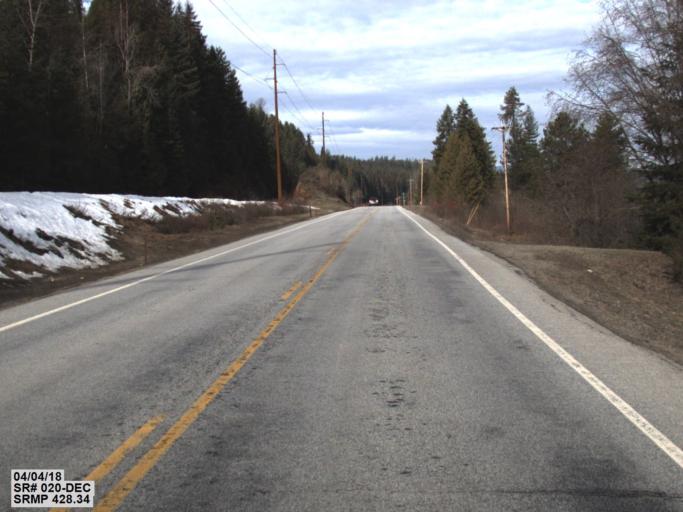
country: US
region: Washington
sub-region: Pend Oreille County
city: Newport
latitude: 48.2310
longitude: -117.1976
